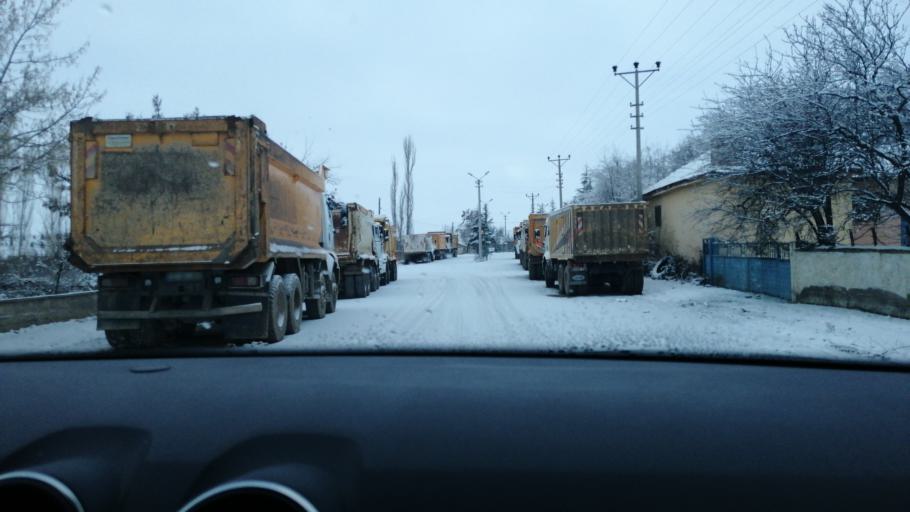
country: TR
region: Aksaray
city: Agacoren
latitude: 38.9313
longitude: 33.9490
